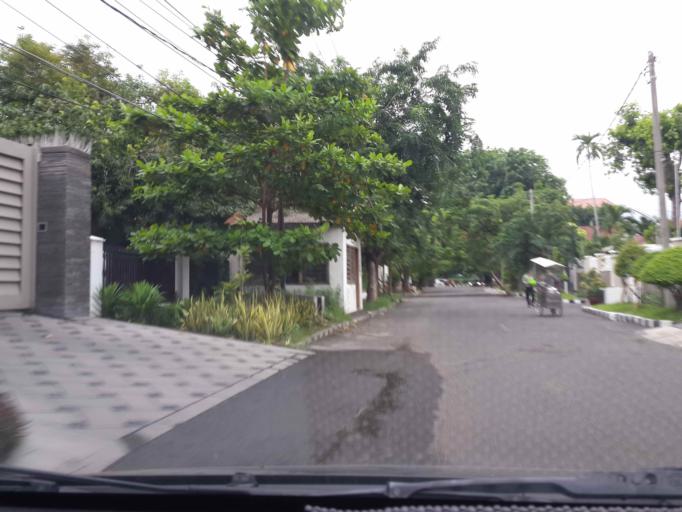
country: ID
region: East Java
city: Gubengairlangga
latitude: -7.2826
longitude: 112.7339
